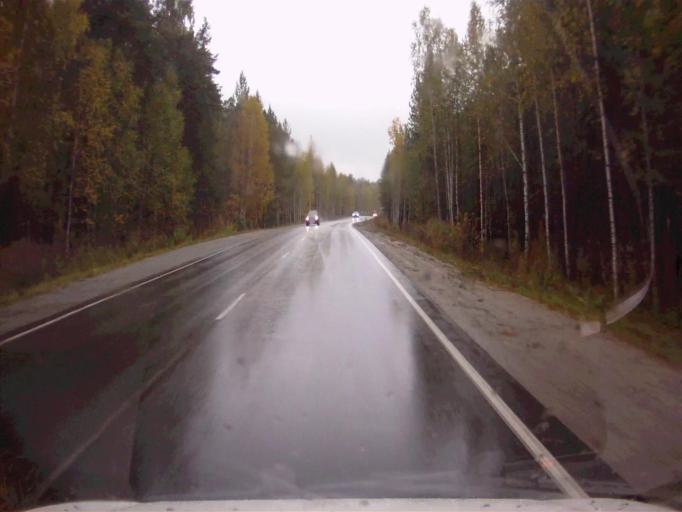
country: RU
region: Chelyabinsk
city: Kyshtym
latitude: 55.6527
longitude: 60.5771
